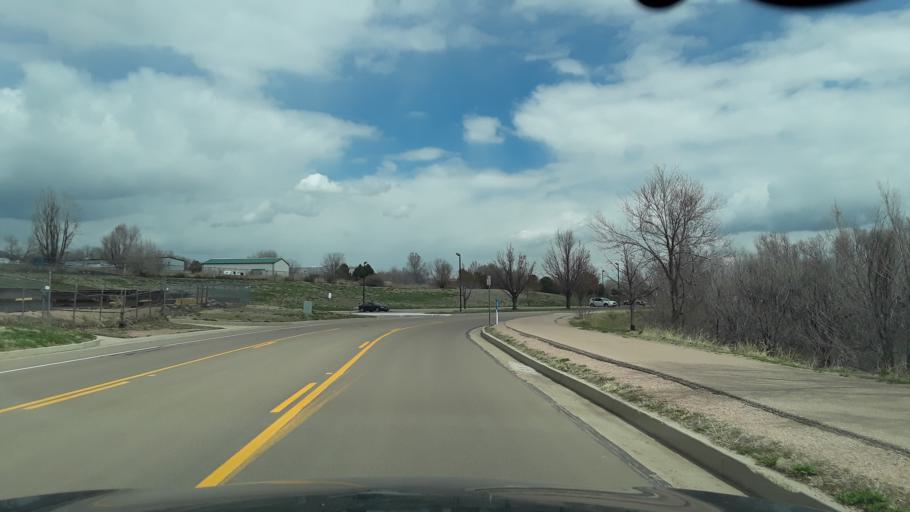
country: US
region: Colorado
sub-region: El Paso County
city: Colorado Springs
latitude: 38.8845
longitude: -104.8295
